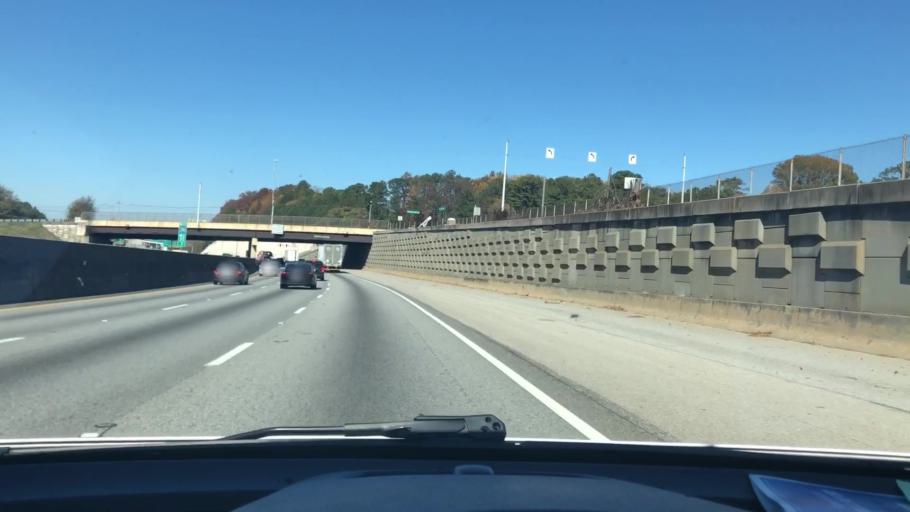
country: US
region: Georgia
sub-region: DeKalb County
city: Doraville
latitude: 33.8841
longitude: -84.2506
